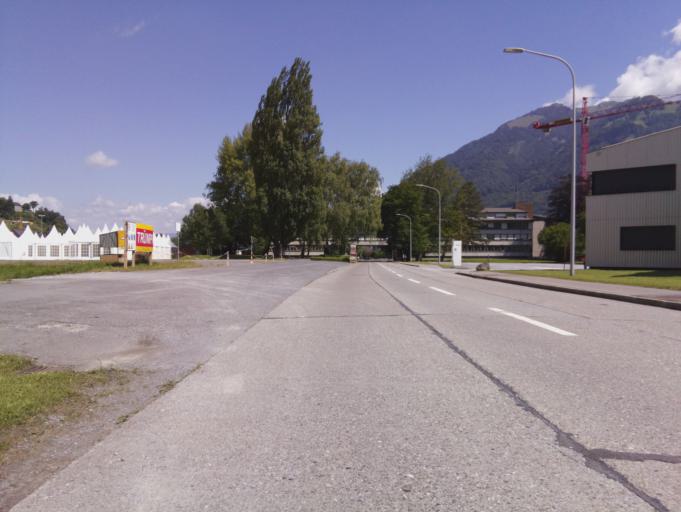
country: CH
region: Glarus
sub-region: Glarus
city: Niederurnen
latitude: 47.1207
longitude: 9.0581
